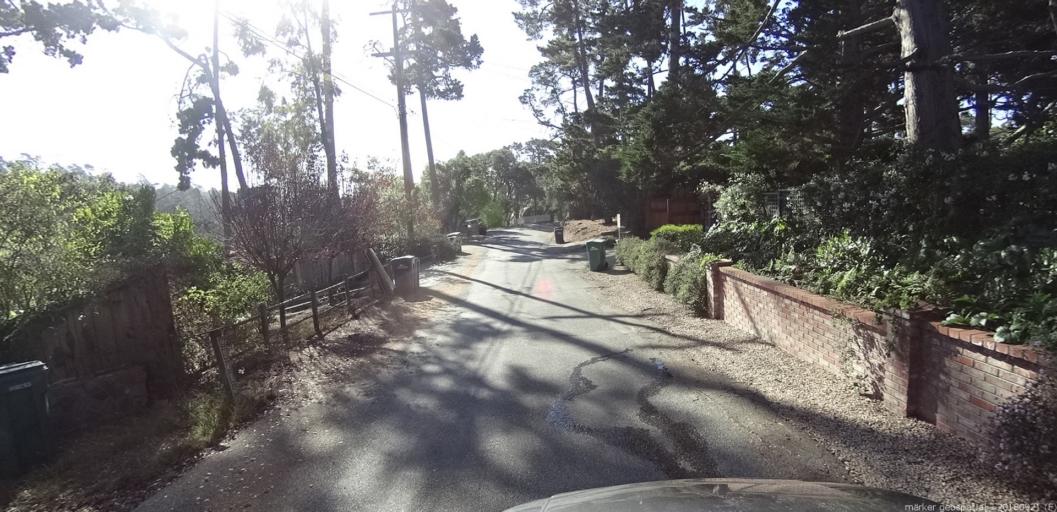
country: US
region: California
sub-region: Monterey County
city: Carmel-by-the-Sea
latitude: 36.5699
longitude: -121.9146
